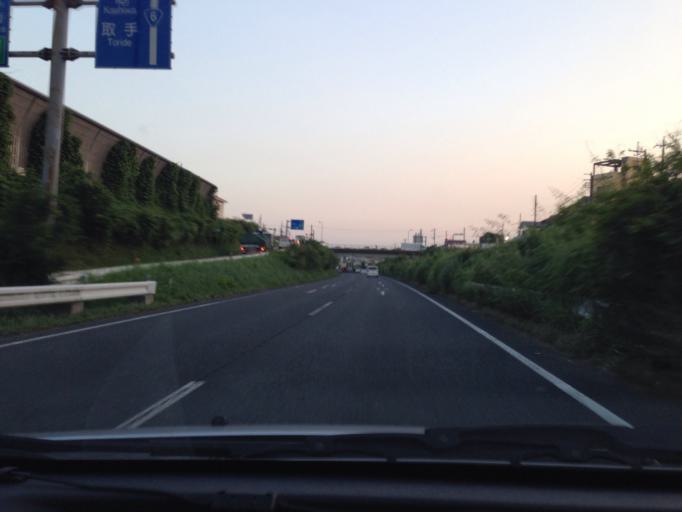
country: JP
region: Ibaraki
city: Naka
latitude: 36.1103
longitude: 140.1991
